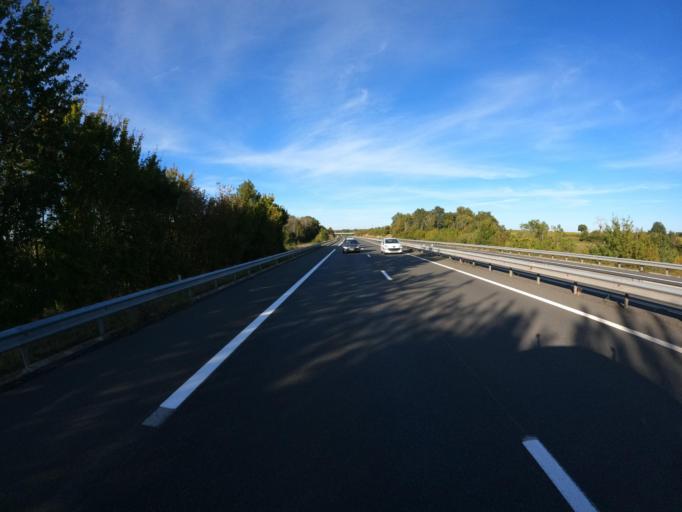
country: FR
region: Pays de la Loire
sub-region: Departement de Maine-et-Loire
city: Saint-Lambert-du-Lattay
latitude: 47.2947
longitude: -0.6118
